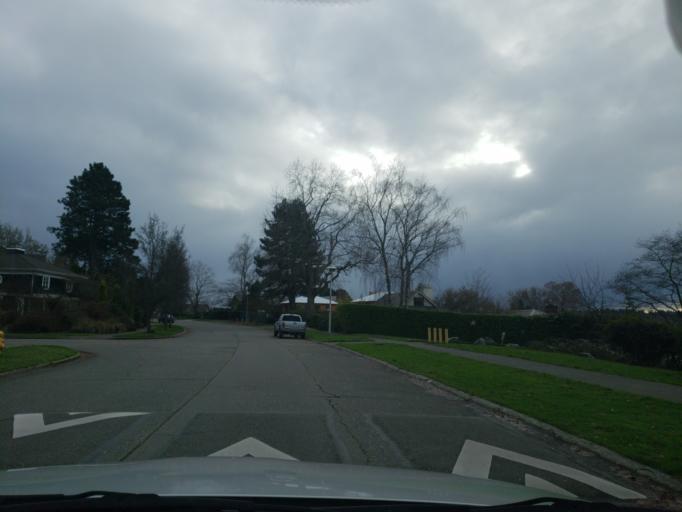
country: US
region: Washington
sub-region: King County
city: Seattle
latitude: 47.6568
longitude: -122.2865
